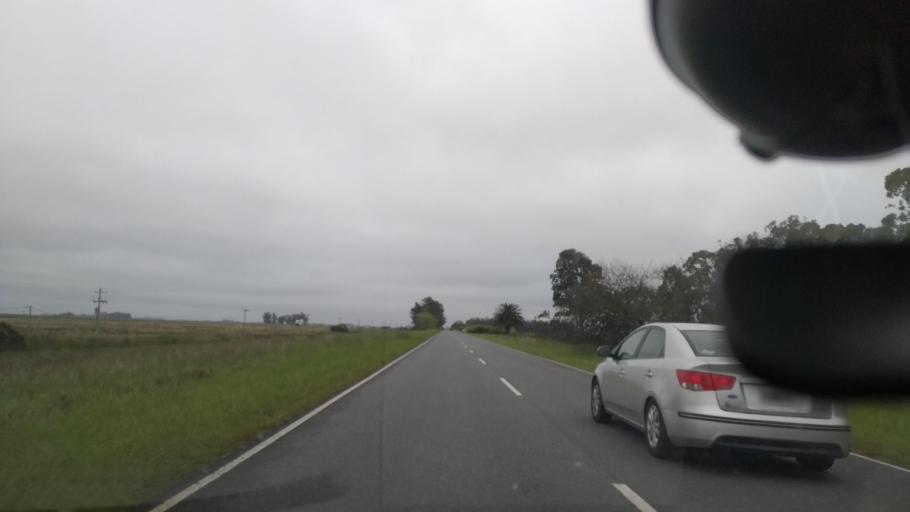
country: AR
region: Buenos Aires
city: Veronica
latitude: -35.4622
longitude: -57.3278
